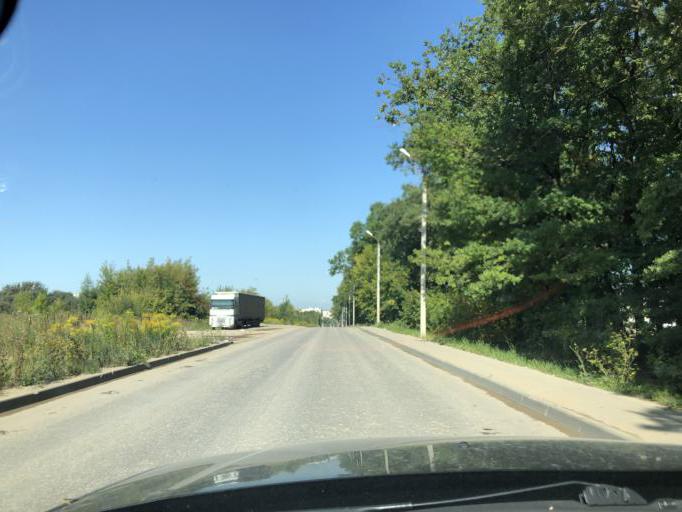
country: RU
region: Tula
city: Tula
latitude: 54.1726
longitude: 37.6523
